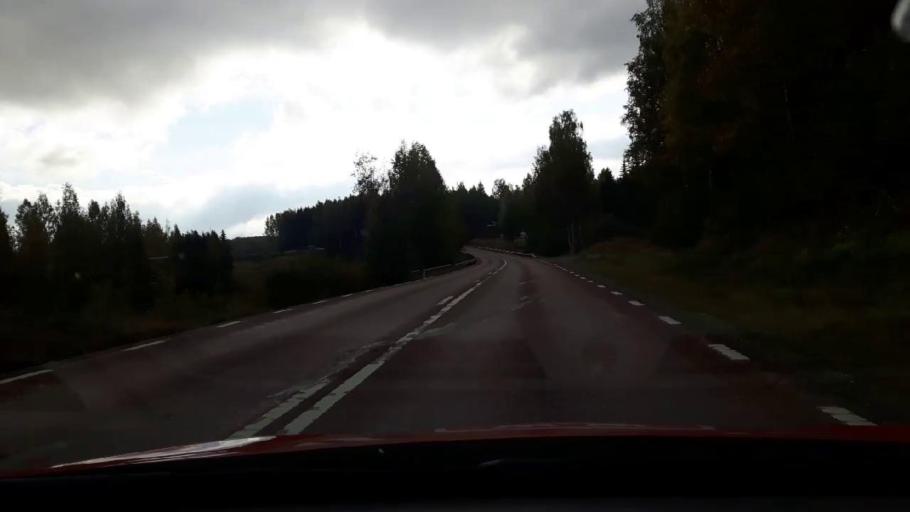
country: SE
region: Gaevleborg
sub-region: Bollnas Kommun
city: Arbra
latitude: 61.5530
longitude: 16.3490
